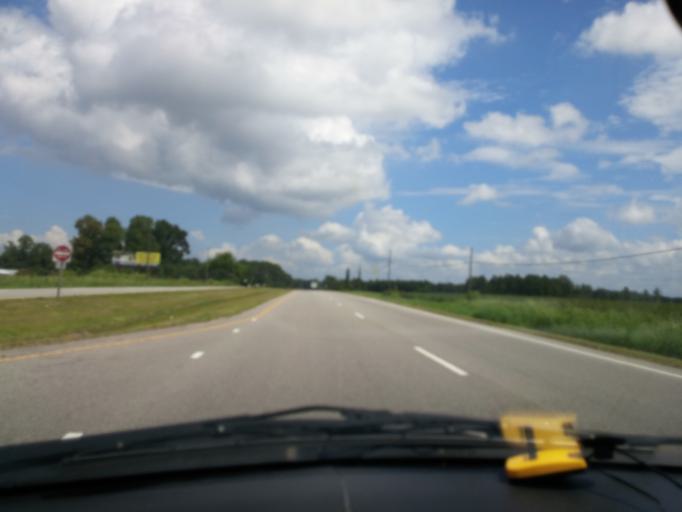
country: US
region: North Carolina
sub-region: Lenoir County
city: Kinston
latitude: 35.2999
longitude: -77.5350
